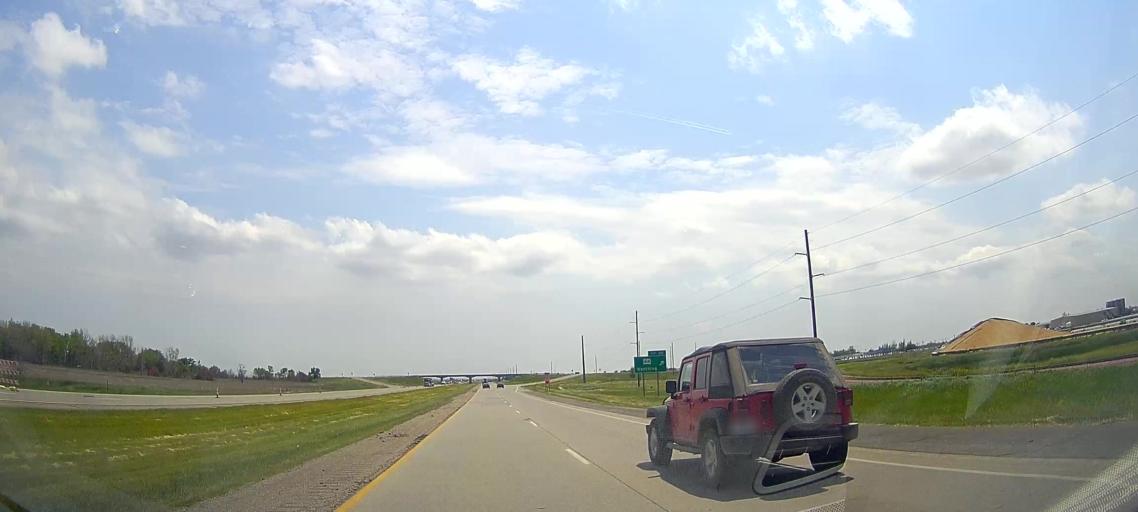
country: US
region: South Dakota
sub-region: Lincoln County
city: Lennox
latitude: 43.3345
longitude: -96.7964
